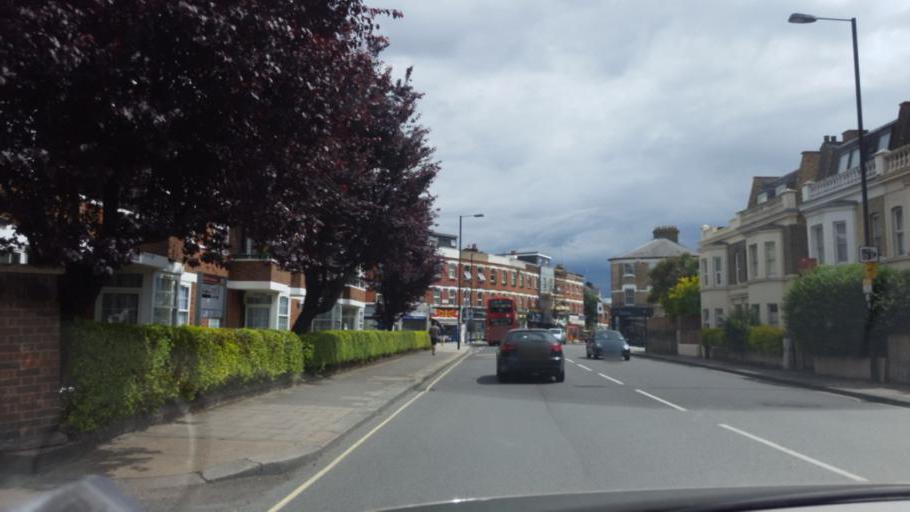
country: GB
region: England
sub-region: Greater London
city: Hammersmith
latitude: 51.5049
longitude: -0.2442
